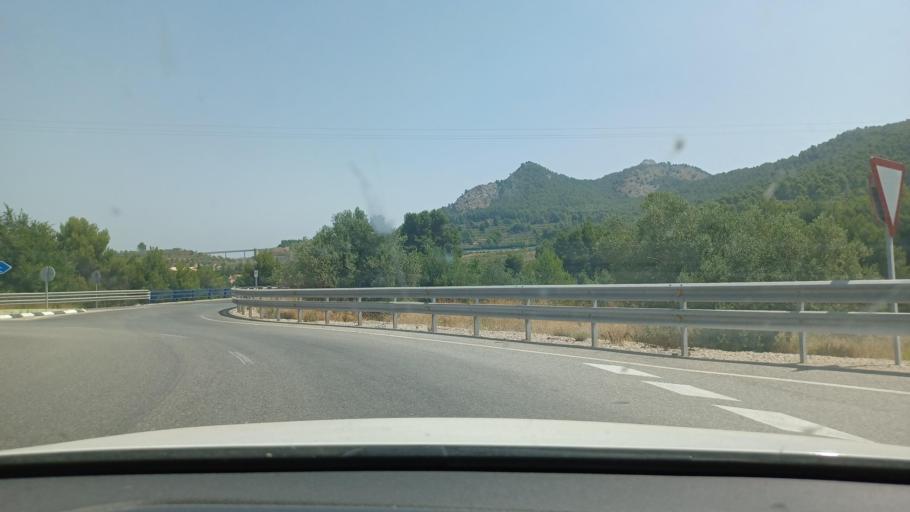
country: ES
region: Valencia
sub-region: Provincia de Alicante
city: Alcoy
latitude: 38.6795
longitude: -0.4663
